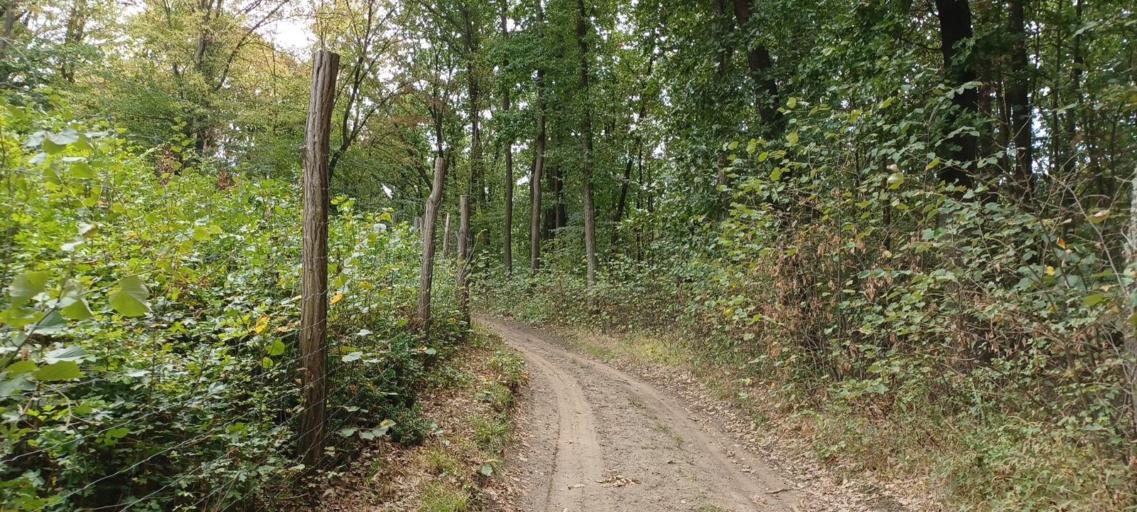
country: HU
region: Tolna
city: Szentgalpuszta
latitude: 46.3331
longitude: 18.6262
